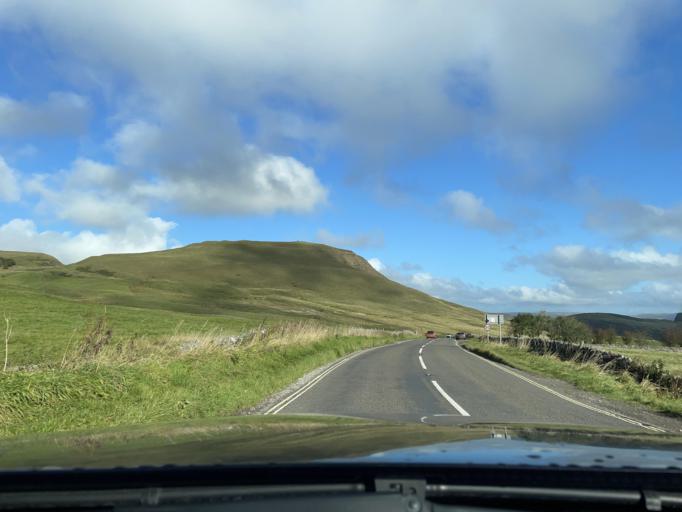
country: GB
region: England
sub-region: Derbyshire
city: High Peak
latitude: 53.3421
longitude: -1.8102
